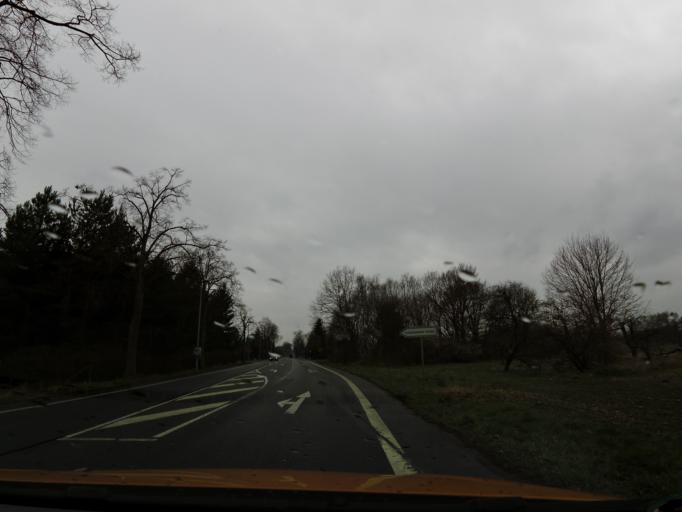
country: DE
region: Brandenburg
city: Gross Kreutz
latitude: 52.4074
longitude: 12.7350
